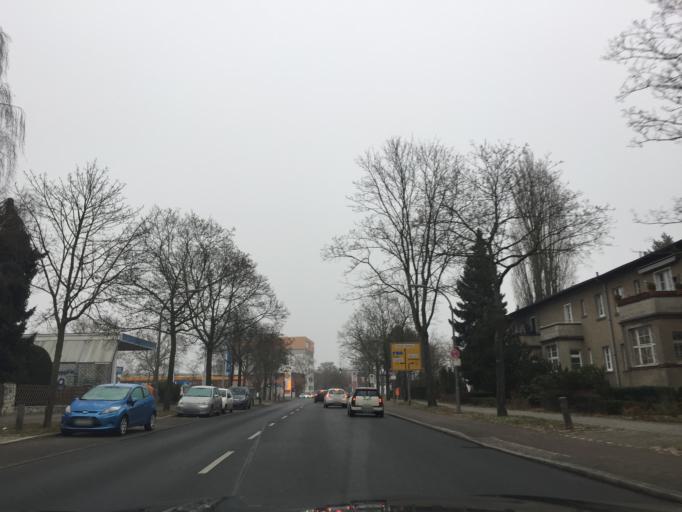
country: DE
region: Berlin
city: Wilhelmstadt
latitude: 52.5158
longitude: 13.1776
